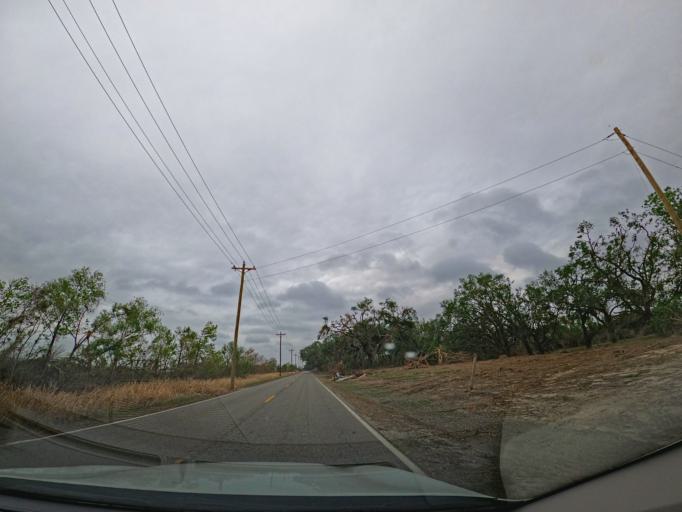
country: US
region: Louisiana
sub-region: Cameron Parish
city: Cameron
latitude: 29.7548
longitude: -92.9197
